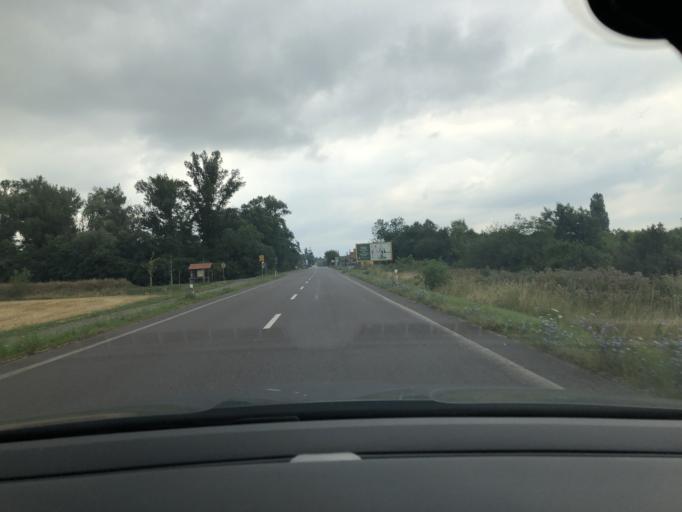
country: CZ
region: South Moravian
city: Hevlin
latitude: 48.7472
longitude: 16.3810
